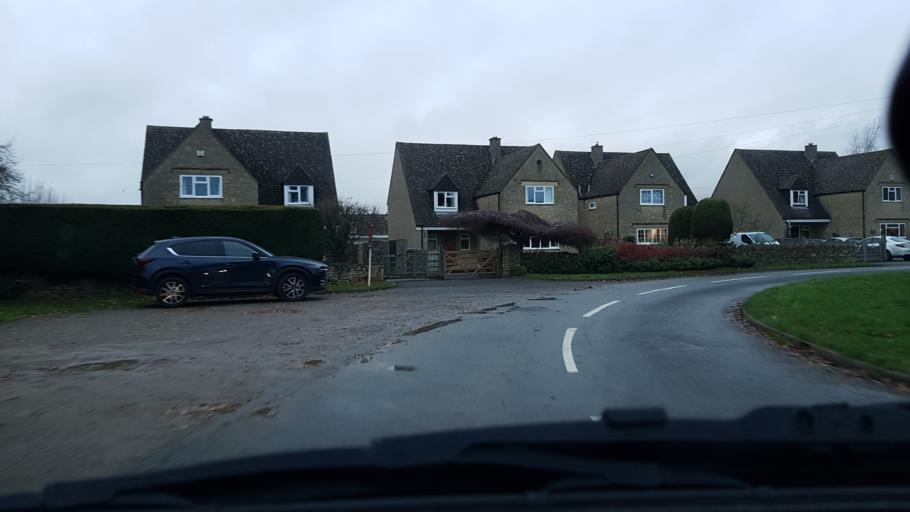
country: GB
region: England
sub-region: Gloucestershire
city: Winchcombe
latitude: 51.9983
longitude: -2.0029
